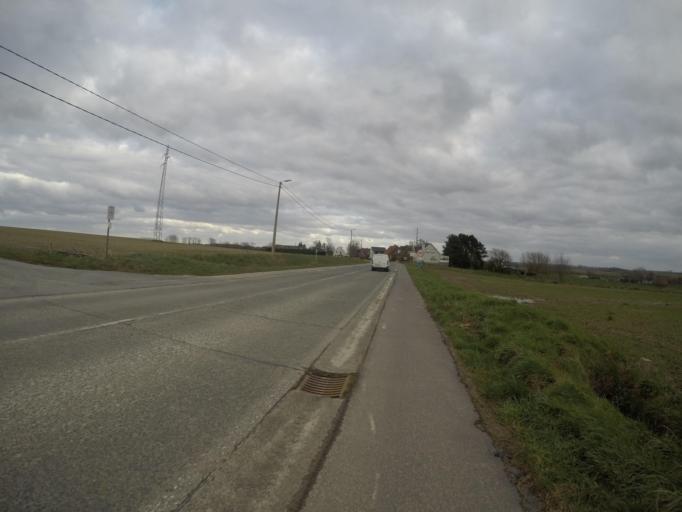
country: BE
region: Flanders
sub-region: Provincie Vlaams-Brabant
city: Pepingen
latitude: 50.7293
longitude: 4.1222
